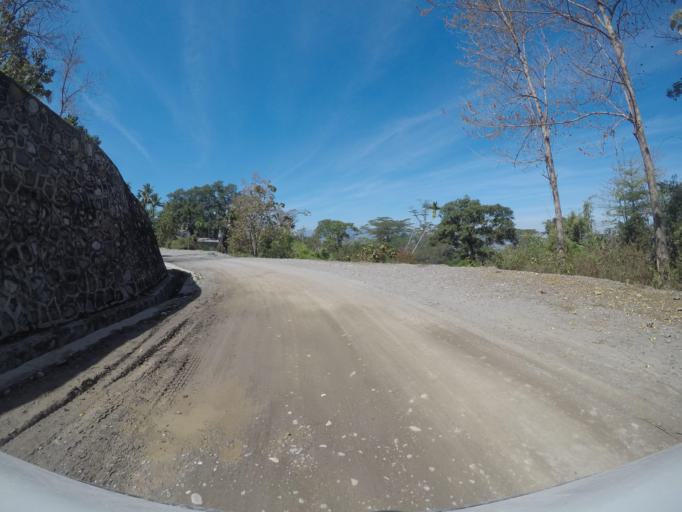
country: TL
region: Ermera
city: Gleno
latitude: -8.8090
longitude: 125.3179
